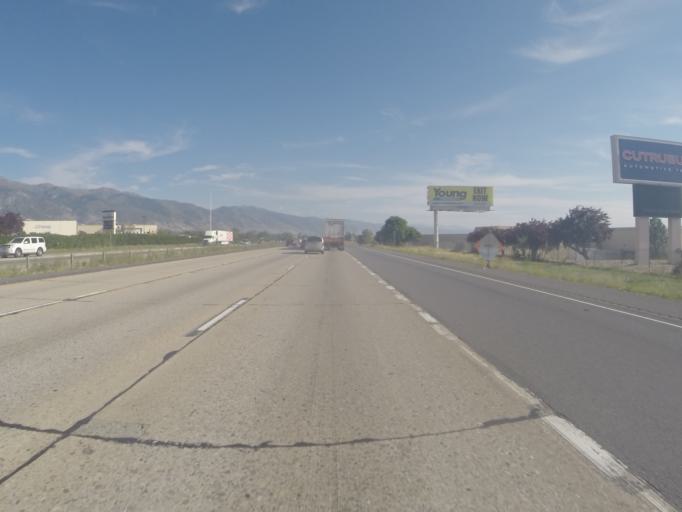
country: US
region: Utah
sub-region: Davis County
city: Layton
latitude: 41.0790
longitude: -111.9816
